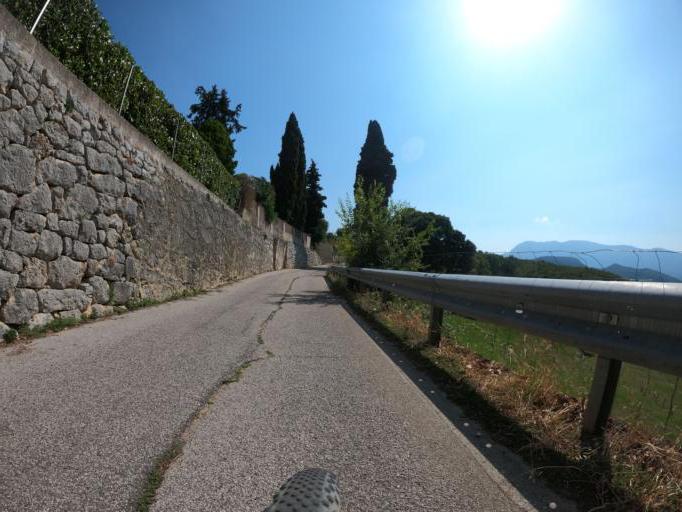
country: IT
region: Veneto
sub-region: Provincia di Verona
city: Caprino Veronese
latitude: 45.6235
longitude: 10.8195
